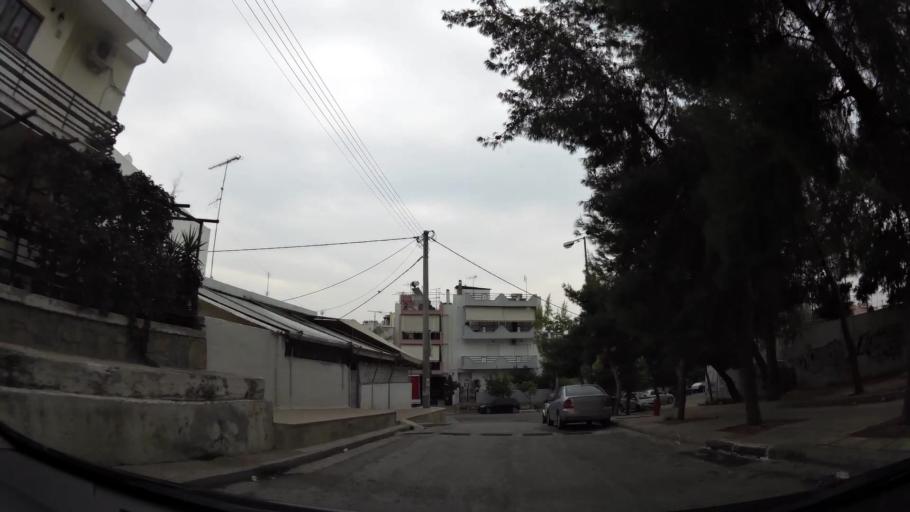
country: GR
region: Attica
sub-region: Nomos Piraios
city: Keratsini
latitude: 37.9773
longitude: 23.6249
